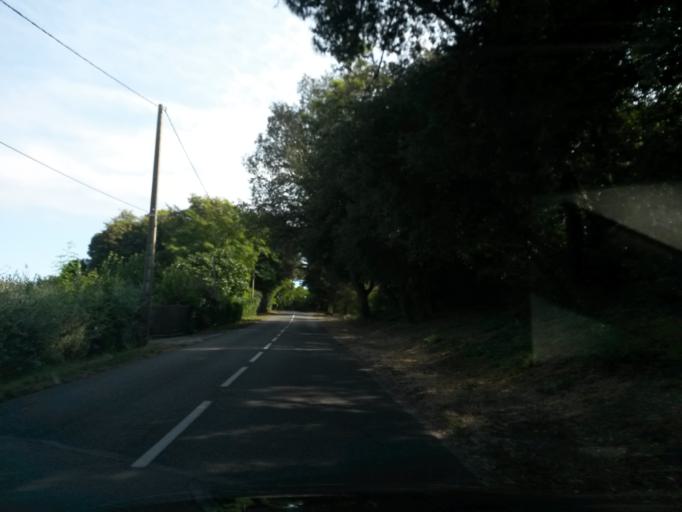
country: FR
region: Pays de la Loire
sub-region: Departement de la Vendee
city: Olonne-sur-Mer
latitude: 46.5405
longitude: -1.8127
